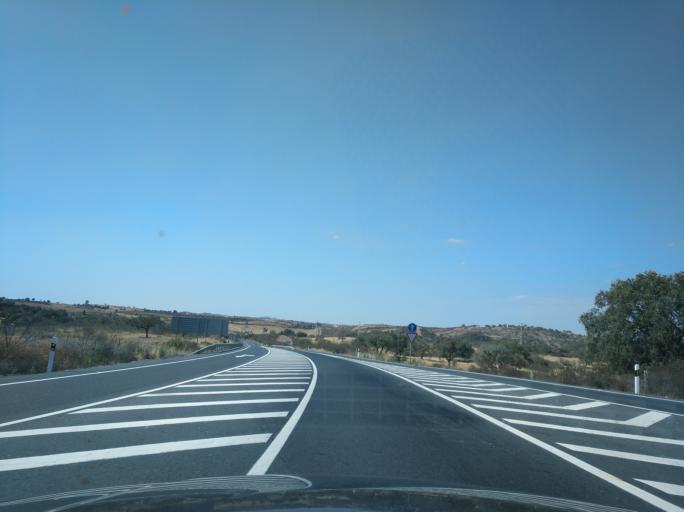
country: ES
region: Andalusia
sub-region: Provincia de Huelva
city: San Bartolome de la Torre
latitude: 37.4671
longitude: -7.1228
